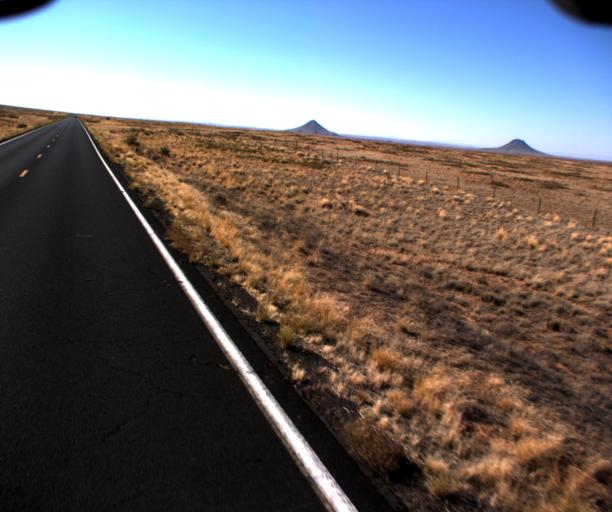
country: US
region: Arizona
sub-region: Navajo County
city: Dilkon
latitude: 35.4375
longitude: -110.4248
